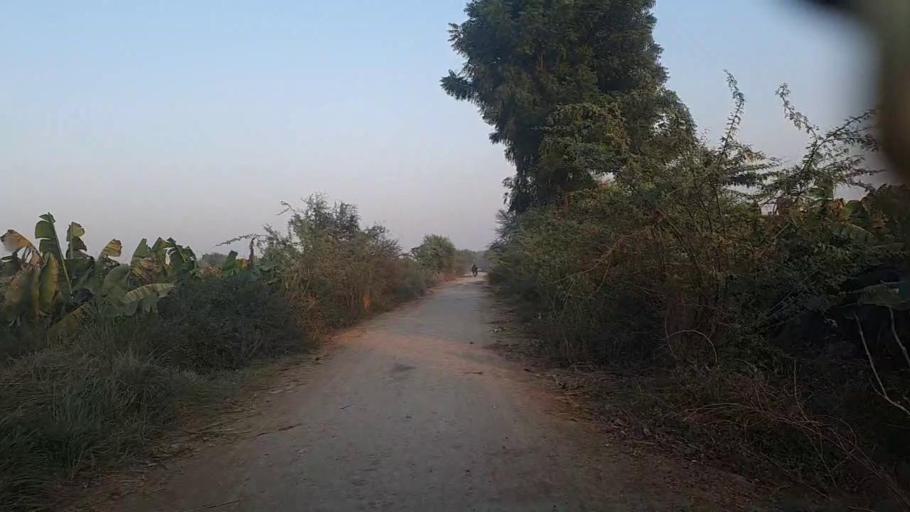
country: PK
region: Sindh
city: Karaundi
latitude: 26.8430
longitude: 68.3561
